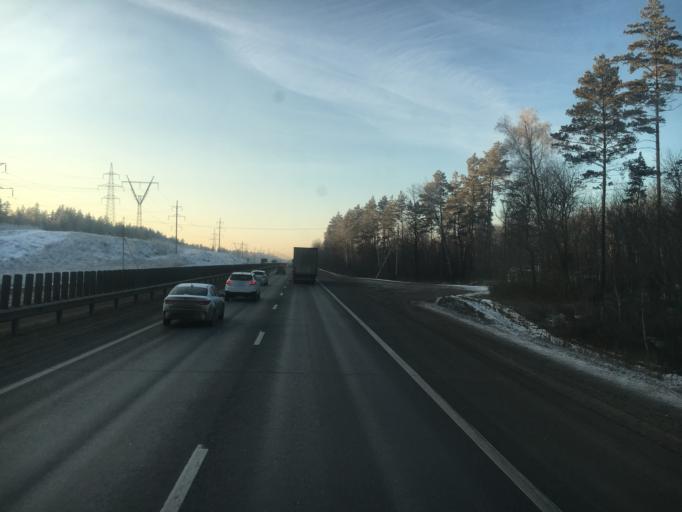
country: RU
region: Samara
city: Pribrezhnyy
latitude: 53.5142
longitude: 49.8958
